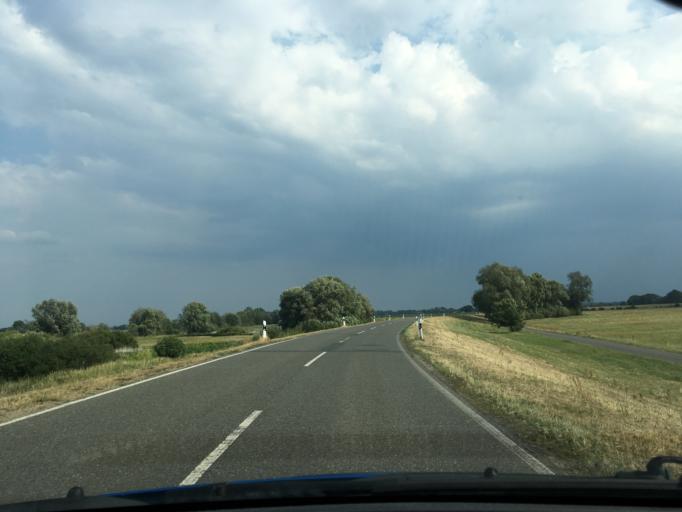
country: DE
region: Lower Saxony
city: Hitzacker
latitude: 53.1462
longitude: 11.0617
